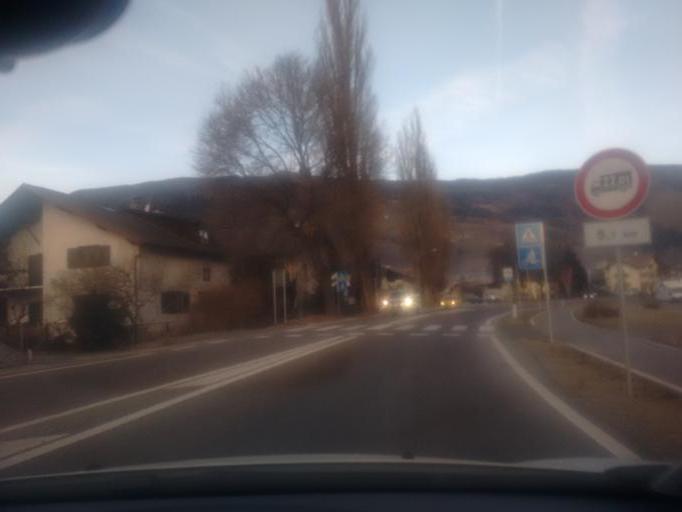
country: IT
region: Trentino-Alto Adige
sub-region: Bolzano
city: Vipiteno
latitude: 46.8913
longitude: 11.4364
